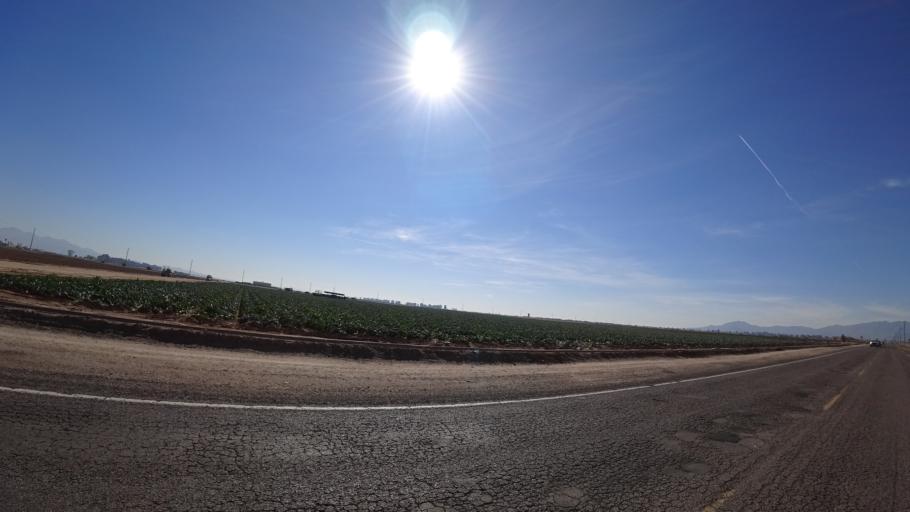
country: US
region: Arizona
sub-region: Maricopa County
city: Citrus Park
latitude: 33.5082
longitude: -112.4332
